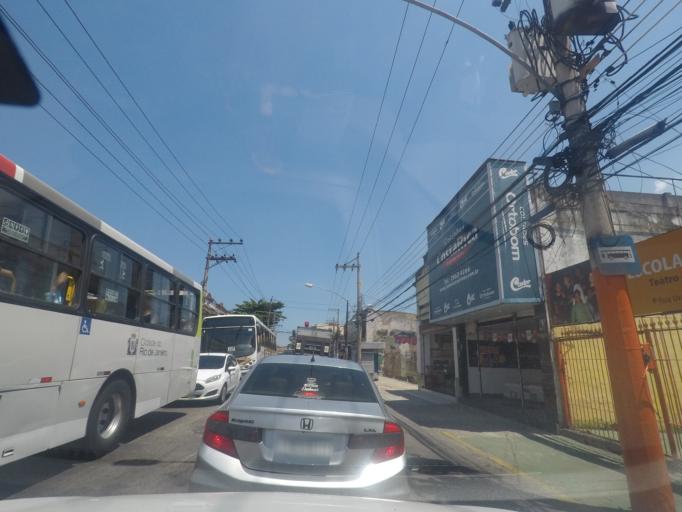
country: BR
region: Rio de Janeiro
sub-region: Duque De Caxias
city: Duque de Caxias
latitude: -22.8492
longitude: -43.2664
